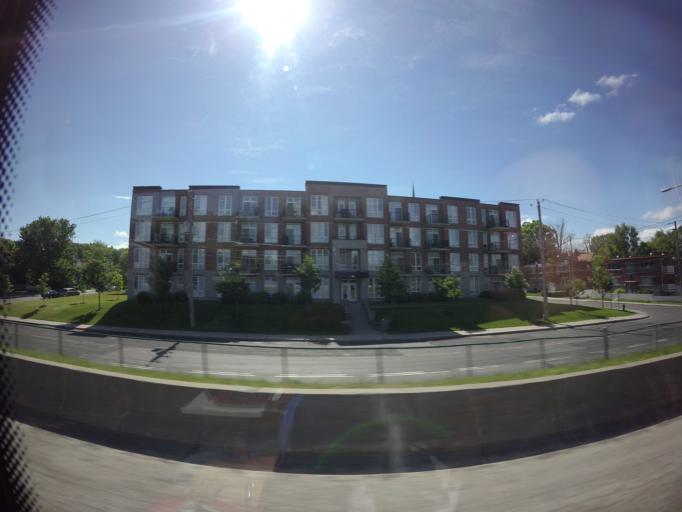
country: CA
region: Quebec
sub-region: Monteregie
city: Longueuil
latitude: 45.5420
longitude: -73.5095
